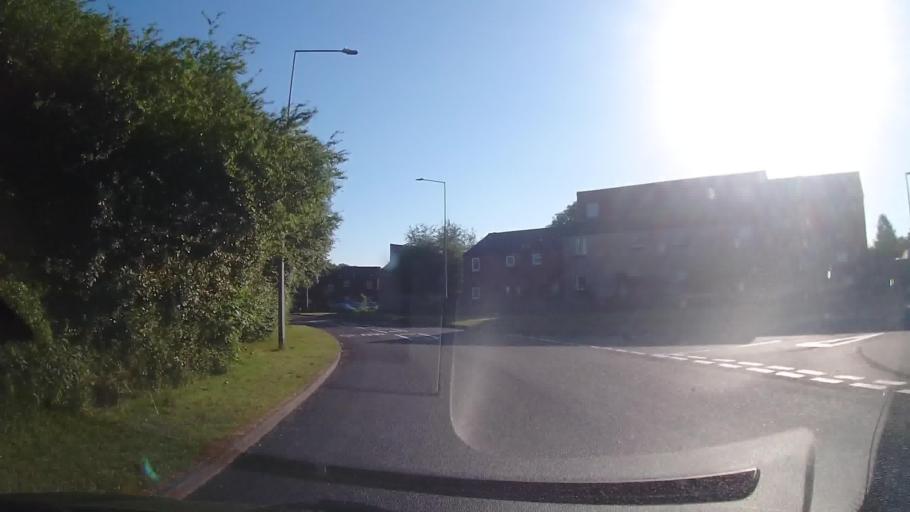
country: GB
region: England
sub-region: Shropshire
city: Hadley
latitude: 52.7049
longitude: -2.4967
